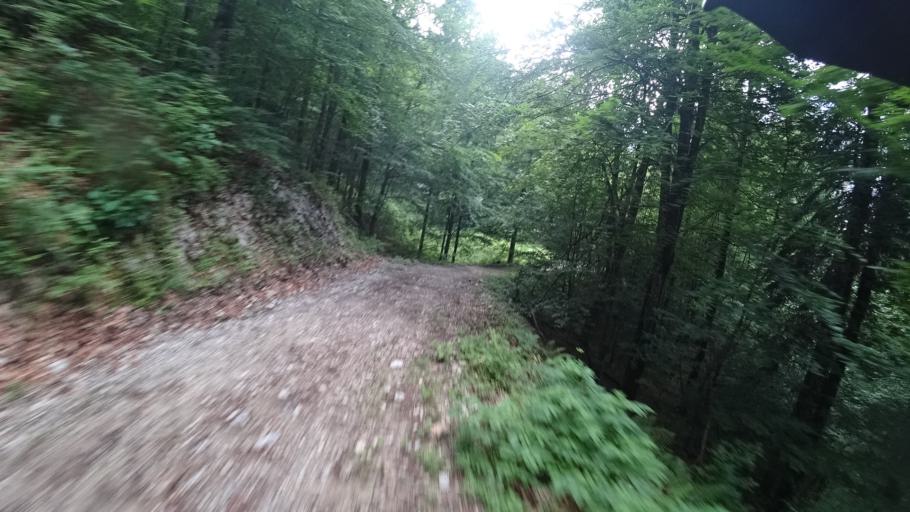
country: SI
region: Osilnica
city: Osilnica
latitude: 45.4911
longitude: 14.6807
